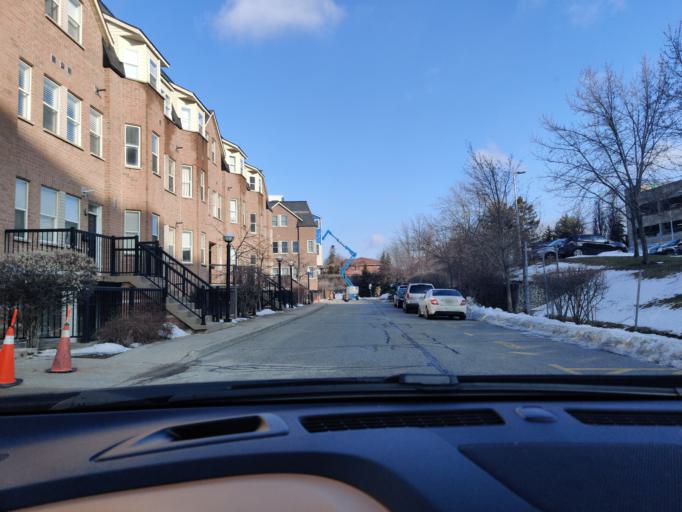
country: CA
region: Ontario
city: Toronto
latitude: 43.7157
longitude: -79.4513
